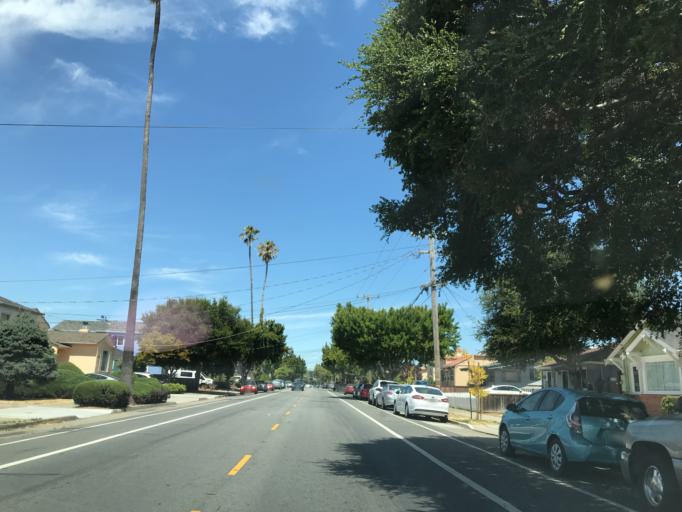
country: US
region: California
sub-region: San Mateo County
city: San Mateo
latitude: 37.5633
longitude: -122.3159
